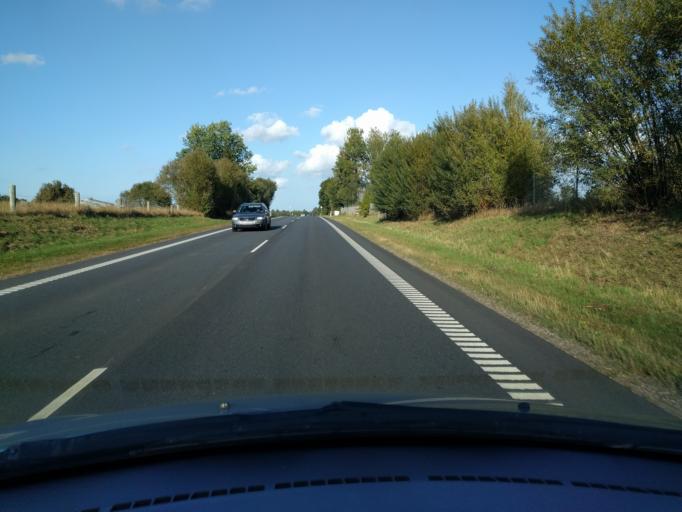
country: DK
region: South Denmark
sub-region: Assens Kommune
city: Tommerup
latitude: 55.3054
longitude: 10.2604
